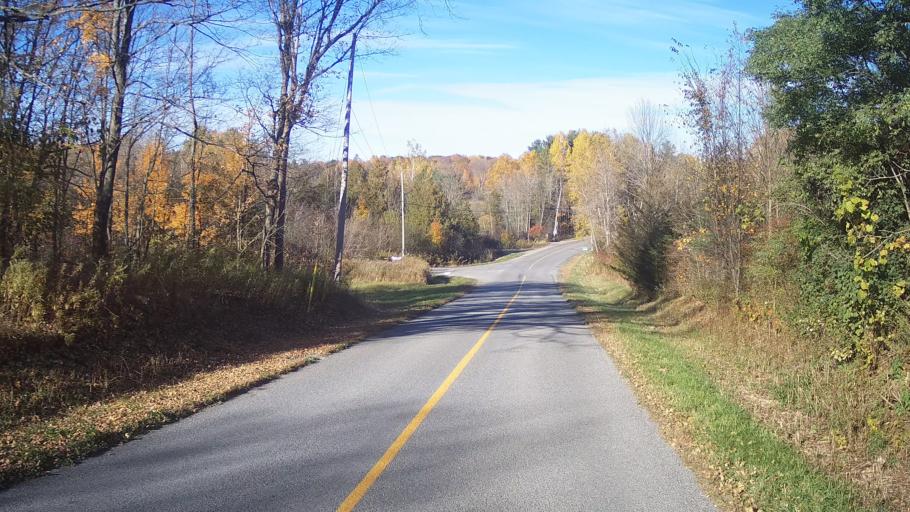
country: CA
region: Ontario
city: Kingston
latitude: 44.4636
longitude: -76.5008
